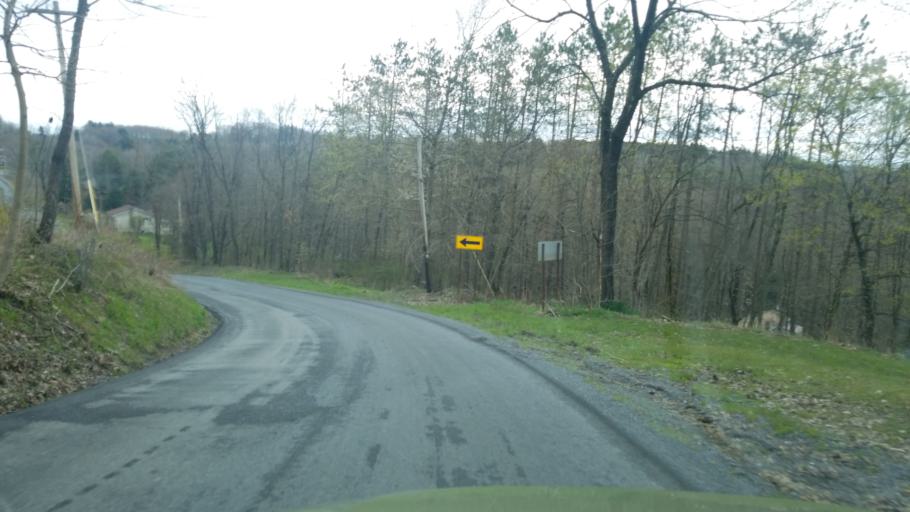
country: US
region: Pennsylvania
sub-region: Clearfield County
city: Clearfield
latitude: 41.0788
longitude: -78.4119
